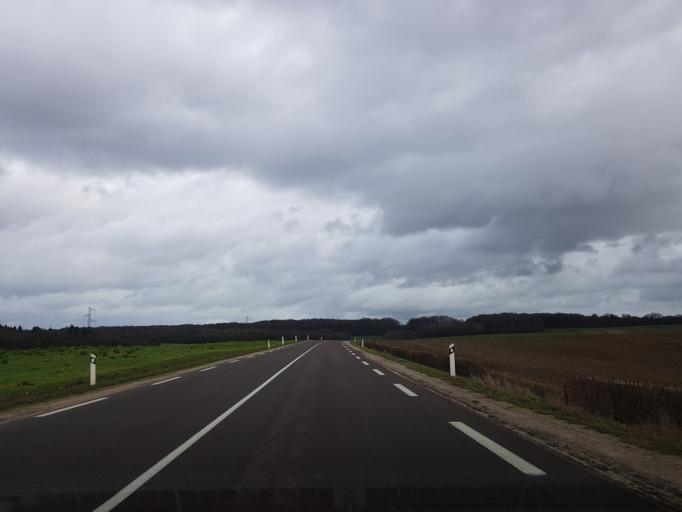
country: FR
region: Franche-Comte
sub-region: Departement de la Haute-Saone
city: Scey-sur-Saone-et-Saint-Albin
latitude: 47.7089
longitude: 5.9138
